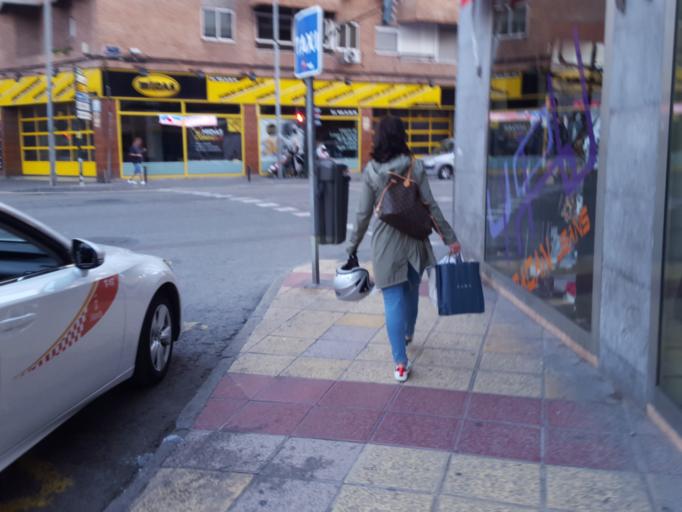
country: ES
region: Murcia
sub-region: Murcia
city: Murcia
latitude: 37.9762
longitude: -1.1332
